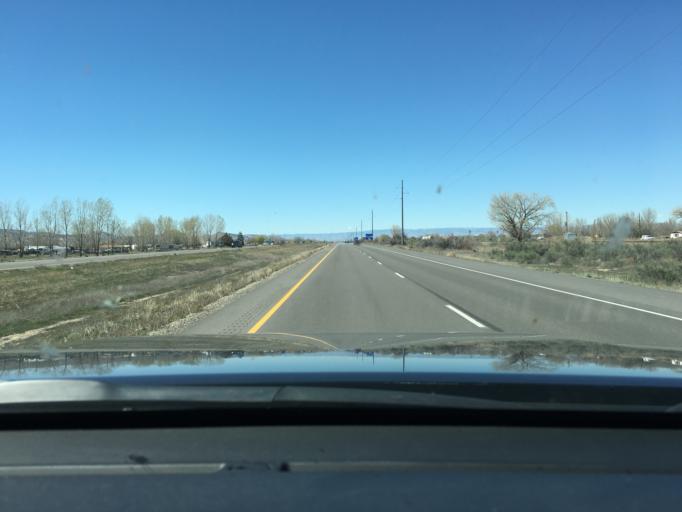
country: US
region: Colorado
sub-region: Mesa County
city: Fruita
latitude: 39.1397
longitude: -108.7047
